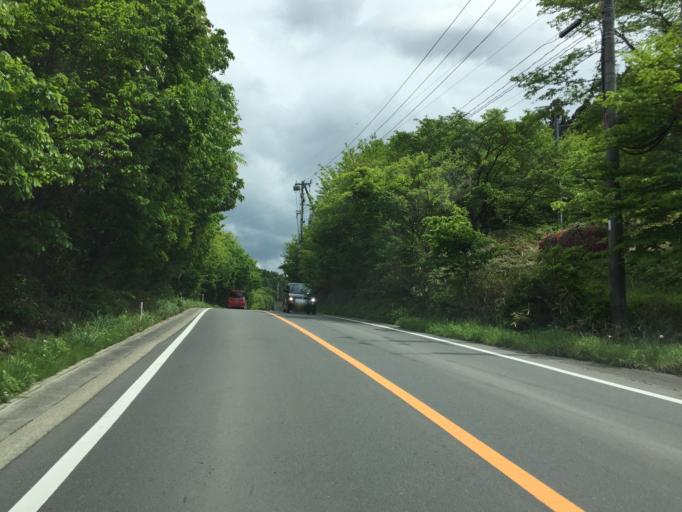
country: JP
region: Fukushima
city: Ishikawa
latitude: 37.0772
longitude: 140.3588
